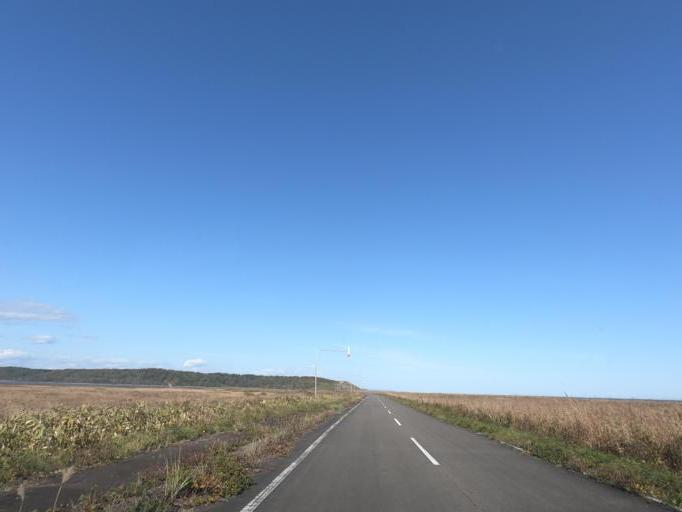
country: JP
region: Hokkaido
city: Obihiro
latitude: 42.5928
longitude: 143.5426
